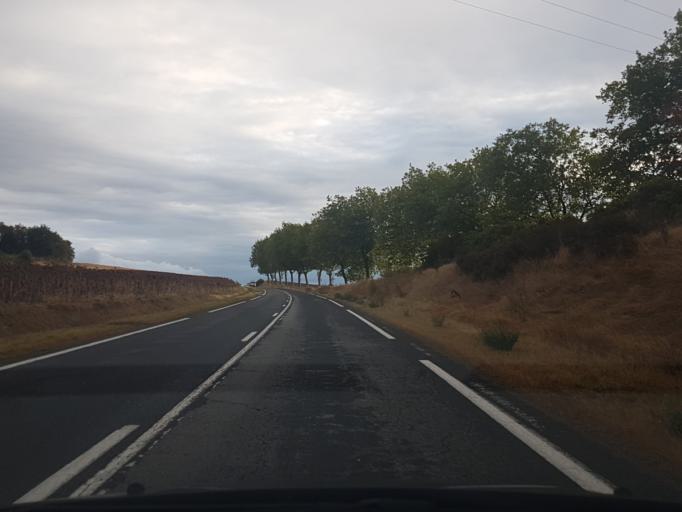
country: FR
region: Languedoc-Roussillon
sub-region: Departement de l'Aude
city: Saint-Martin-Lalande
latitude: 43.1682
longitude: 1.9973
